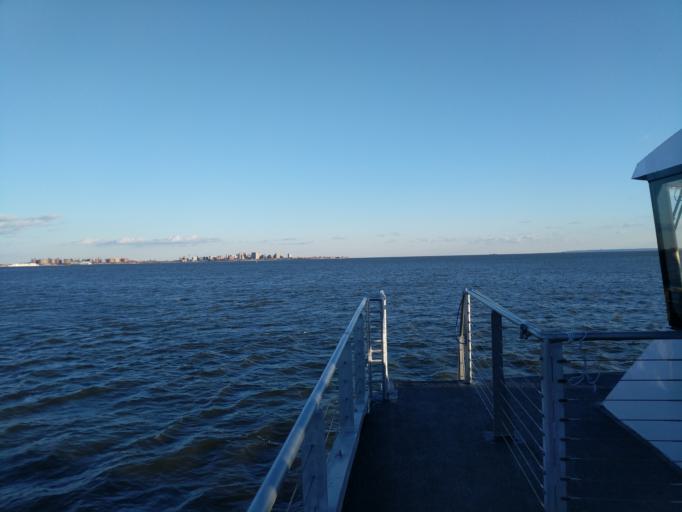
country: US
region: New York
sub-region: Kings County
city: Bensonhurst
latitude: 40.6054
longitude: -74.0382
